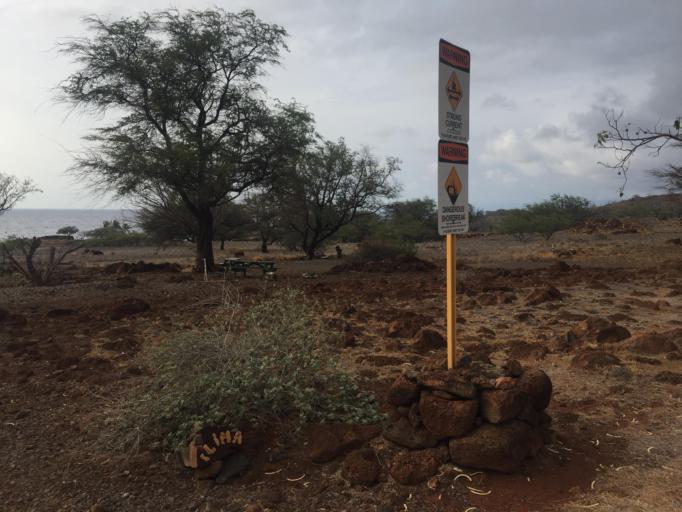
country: US
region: Hawaii
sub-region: Hawaii County
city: Hawi
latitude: 20.1753
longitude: -155.8976
